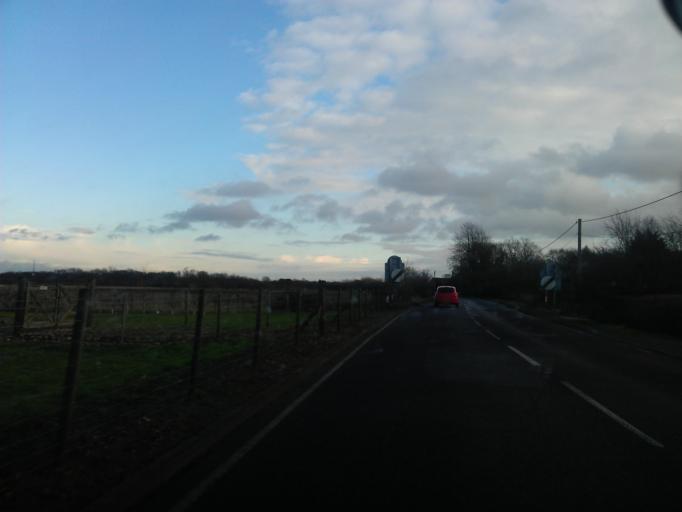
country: GB
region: England
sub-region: Essex
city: Alresford
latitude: 51.8806
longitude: 1.0011
